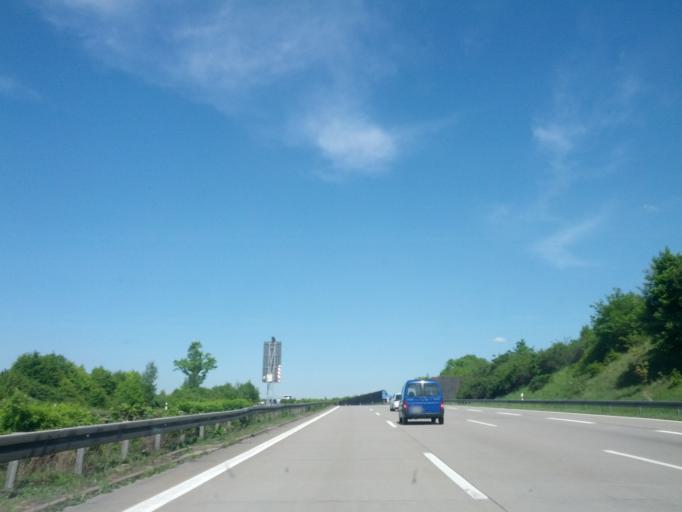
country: DE
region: Saxony
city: Frankenberg
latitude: 50.9258
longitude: 13.0487
